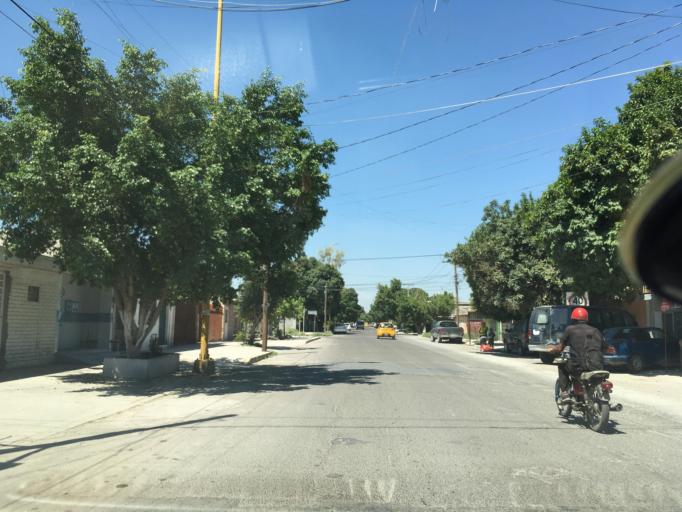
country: MX
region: Coahuila
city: Torreon
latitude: 25.5124
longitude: -103.4305
